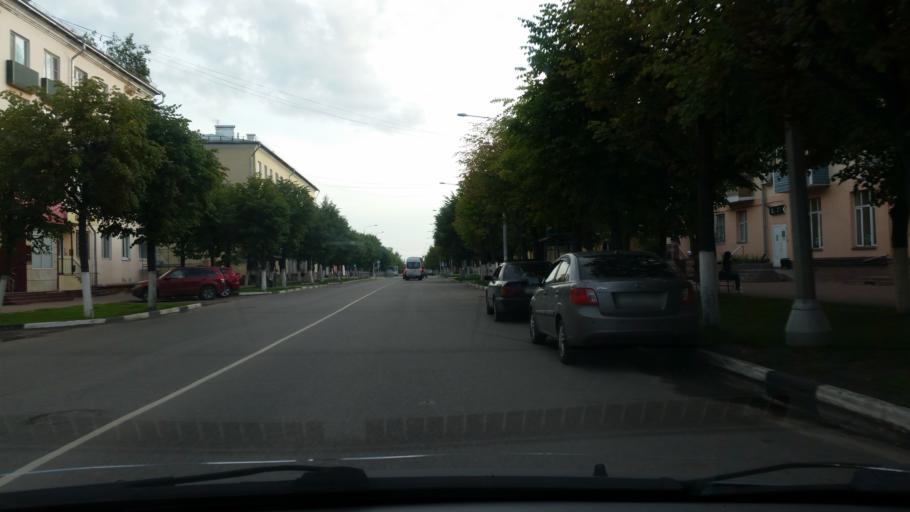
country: RU
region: Moskovskaya
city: Serpukhov
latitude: 54.9233
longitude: 37.4315
